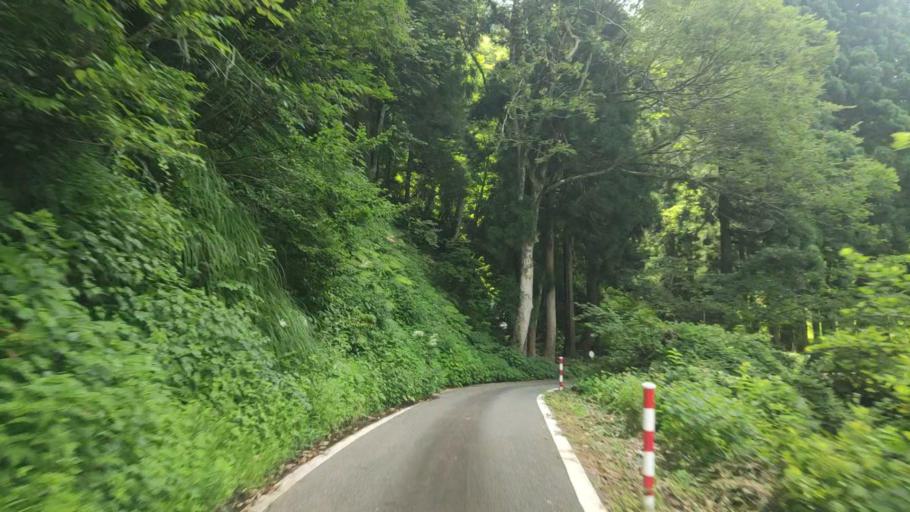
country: JP
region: Fukui
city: Katsuyama
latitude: 36.1920
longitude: 136.5260
